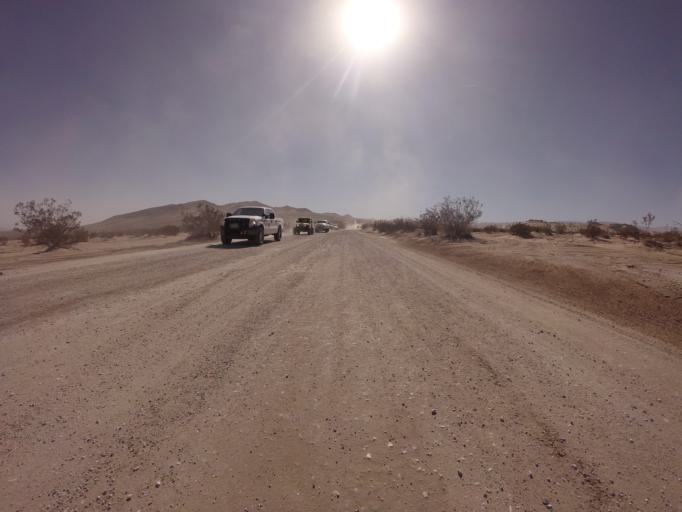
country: US
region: California
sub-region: San Bernardino County
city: Yucca Valley
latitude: 34.3915
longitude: -116.5258
